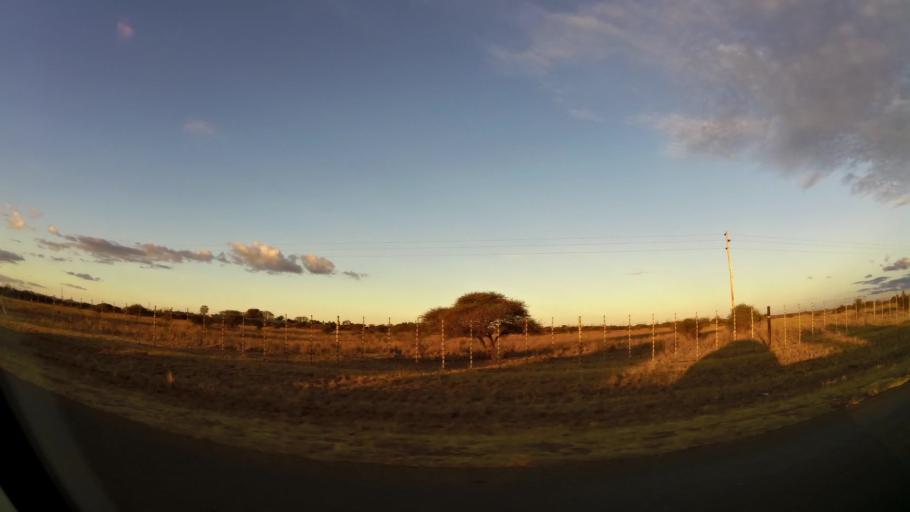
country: ZA
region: Limpopo
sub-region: Capricorn District Municipality
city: Polokwane
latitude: -23.8211
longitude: 29.4817
